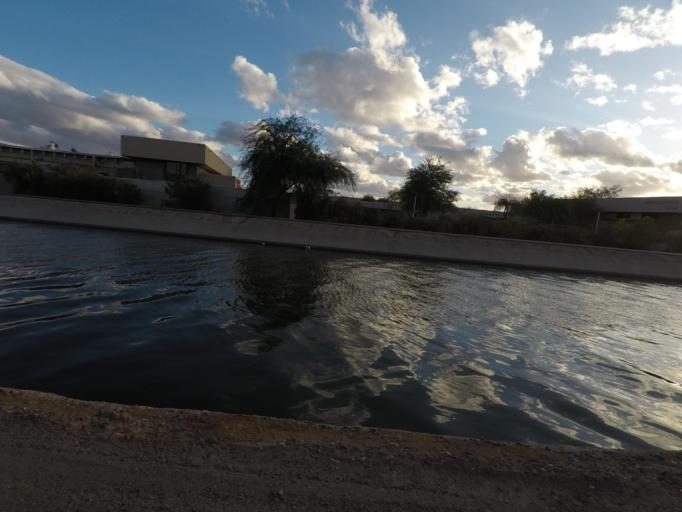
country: US
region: Arizona
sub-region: Maricopa County
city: Glendale
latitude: 33.4899
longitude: -112.1377
